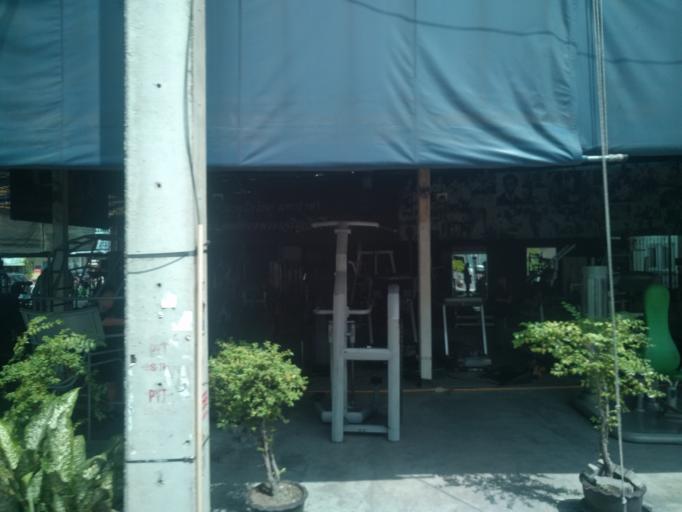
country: TH
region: Chon Buri
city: Phatthaya
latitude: 12.9235
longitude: 100.8825
